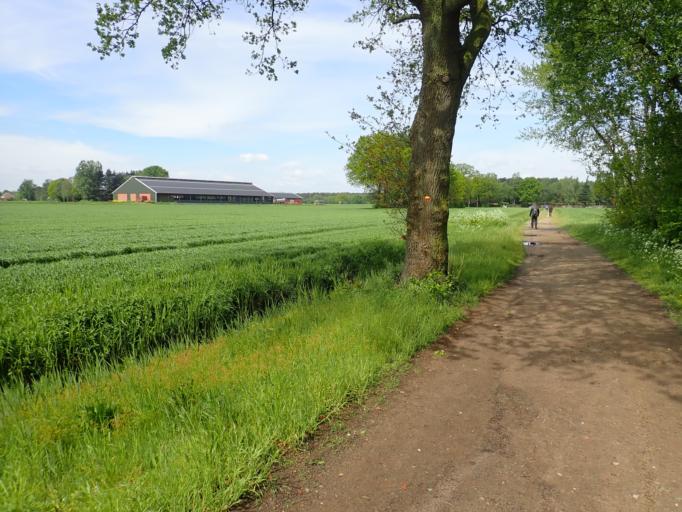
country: BE
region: Flanders
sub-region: Provincie Antwerpen
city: Lille
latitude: 51.2109
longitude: 4.8354
